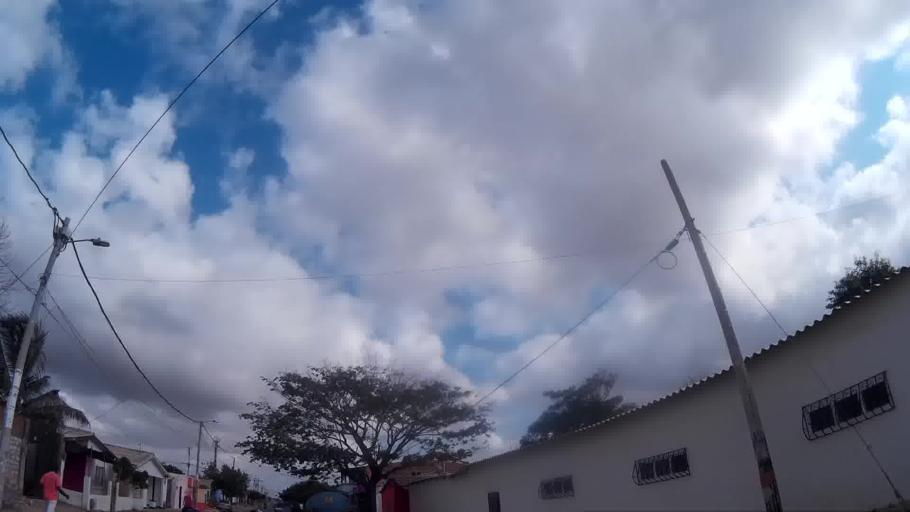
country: CO
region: La Guajira
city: Maicao
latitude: 11.3838
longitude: -72.2381
